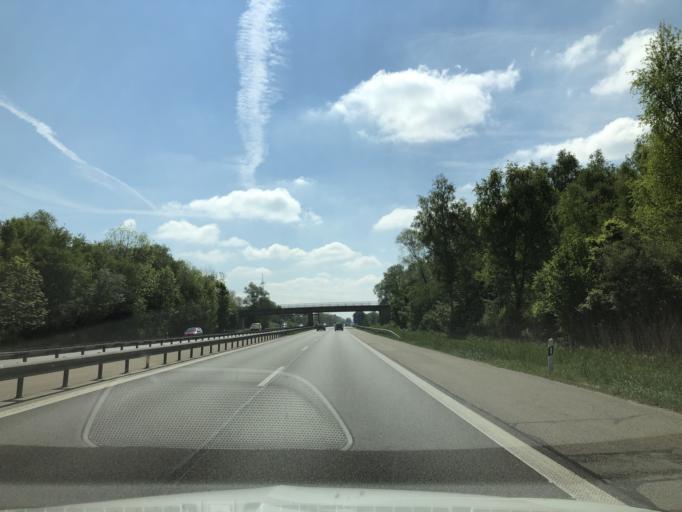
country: DE
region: Bavaria
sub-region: Upper Bavaria
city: Grobenzell
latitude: 48.2057
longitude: 11.3952
